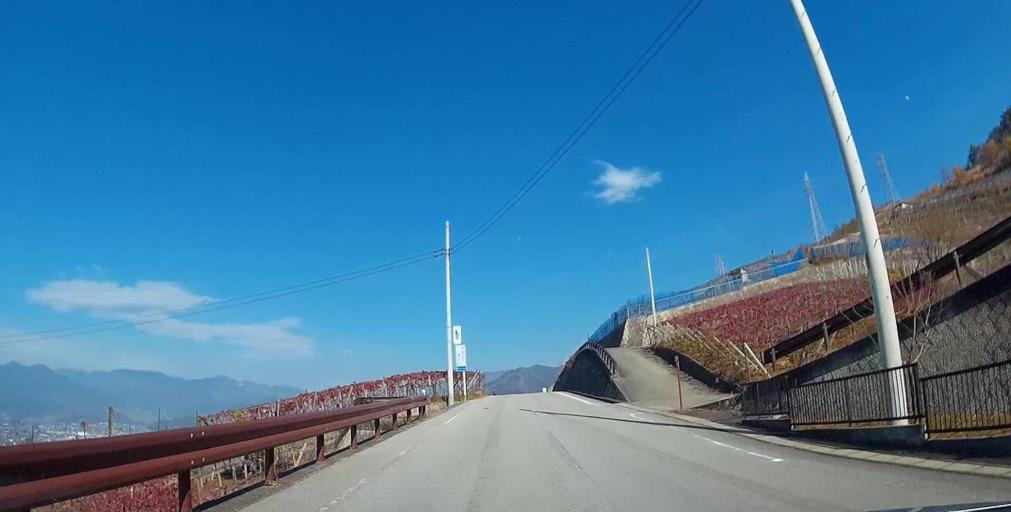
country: JP
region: Yamanashi
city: Enzan
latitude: 35.6614
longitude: 138.7373
